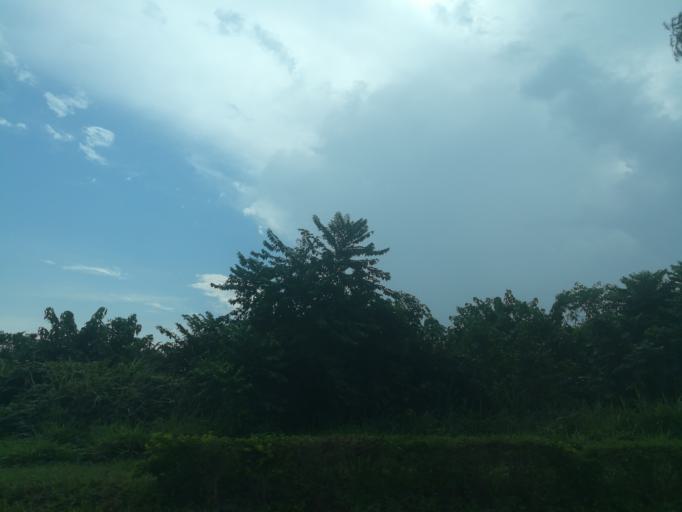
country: NG
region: Lagos
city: Ikorodu
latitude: 6.6382
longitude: 3.5213
